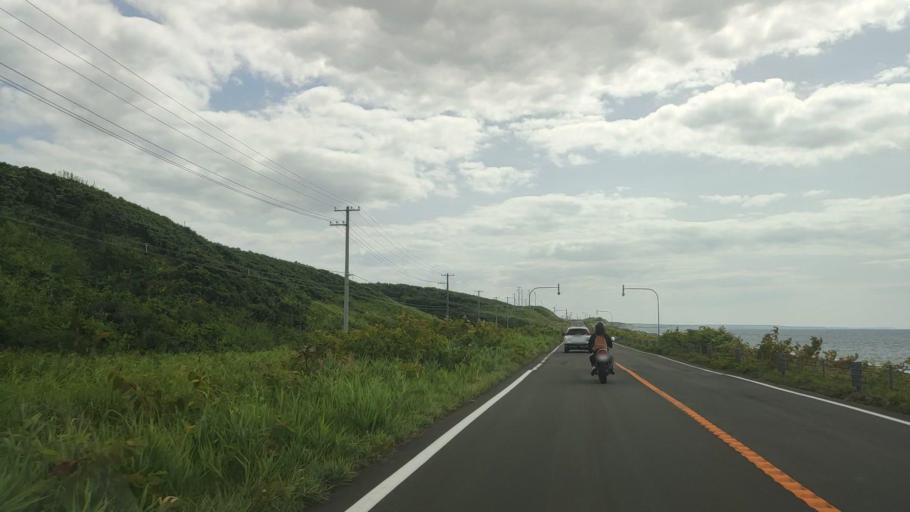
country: JP
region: Hokkaido
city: Rumoi
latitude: 44.5074
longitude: 141.7648
